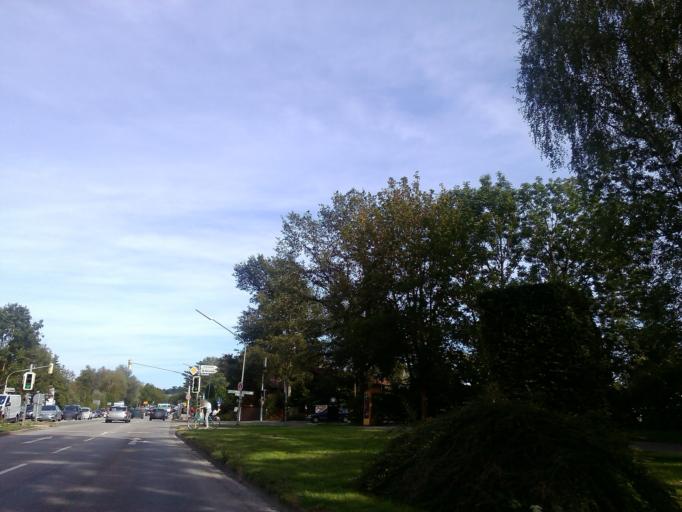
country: DE
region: Bavaria
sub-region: Upper Bavaria
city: Starnberg
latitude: 48.0004
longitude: 11.3528
